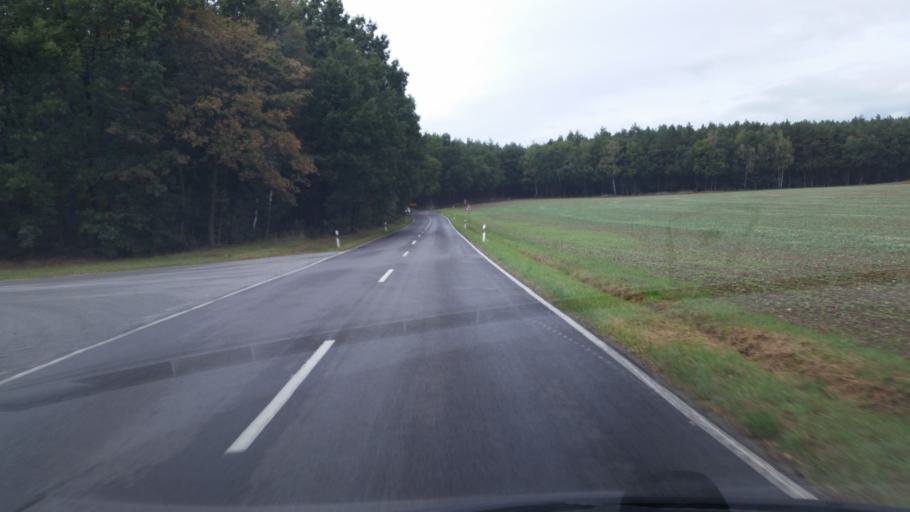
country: DE
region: Saxony
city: Kamenz
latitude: 51.2977
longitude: 14.0516
